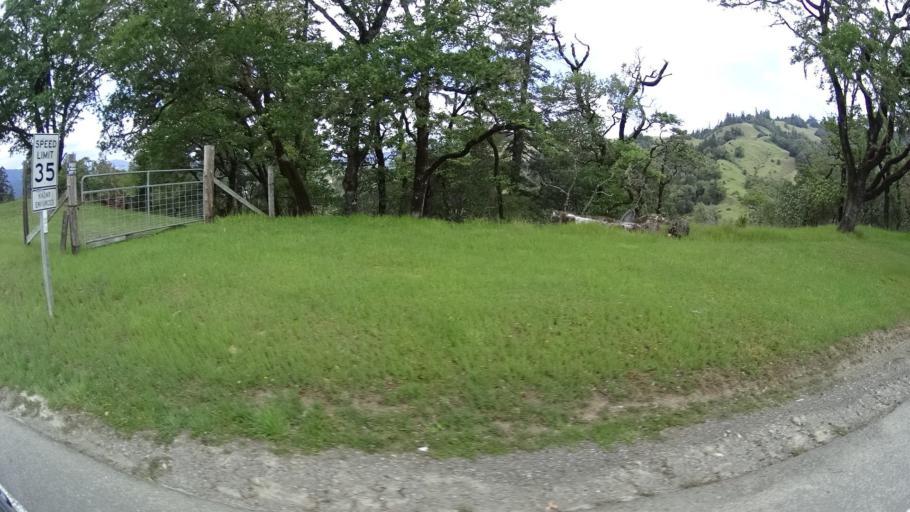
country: US
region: California
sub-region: Humboldt County
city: Redway
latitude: 40.1112
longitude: -123.7837
